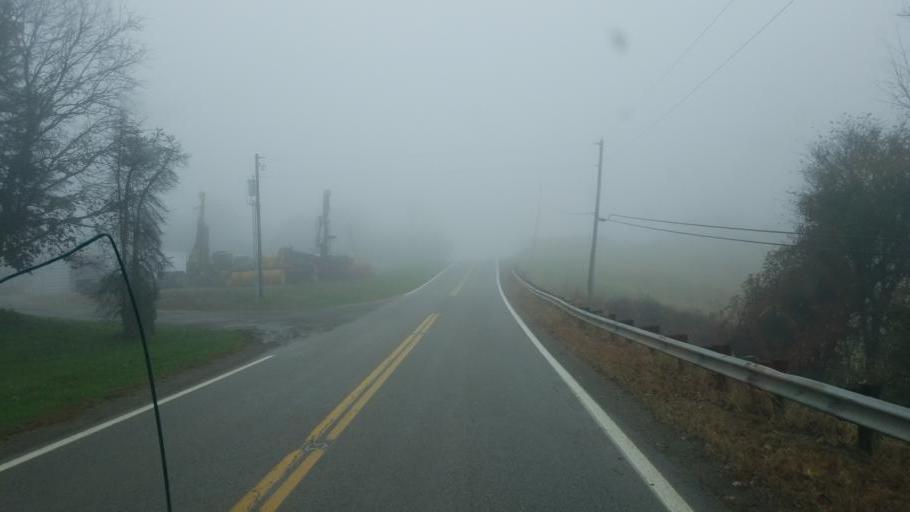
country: US
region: Ohio
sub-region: Morgan County
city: McConnelsville
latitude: 39.5803
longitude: -81.8597
